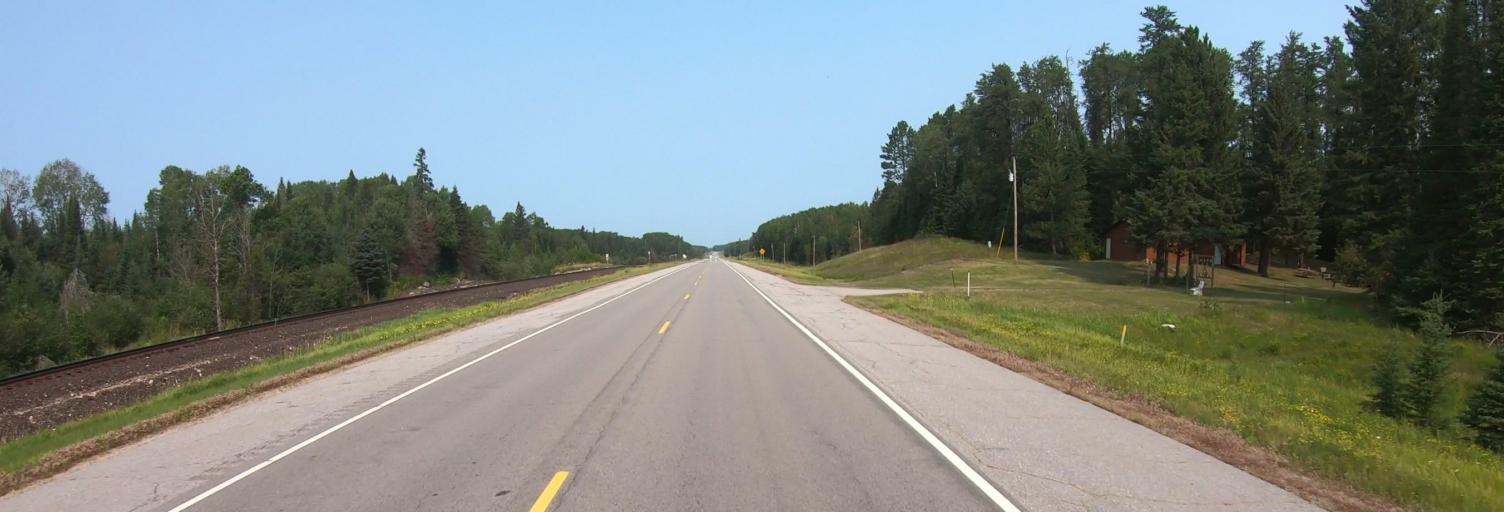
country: US
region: Minnesota
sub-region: Saint Louis County
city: Chisholm
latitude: 48.1501
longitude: -92.8665
